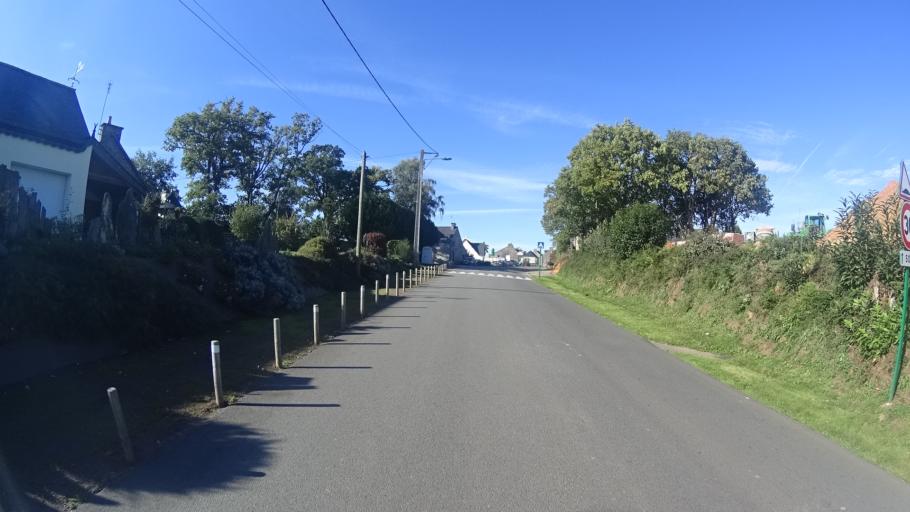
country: FR
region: Brittany
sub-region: Departement du Morbihan
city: Peillac
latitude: 47.7381
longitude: -2.2120
